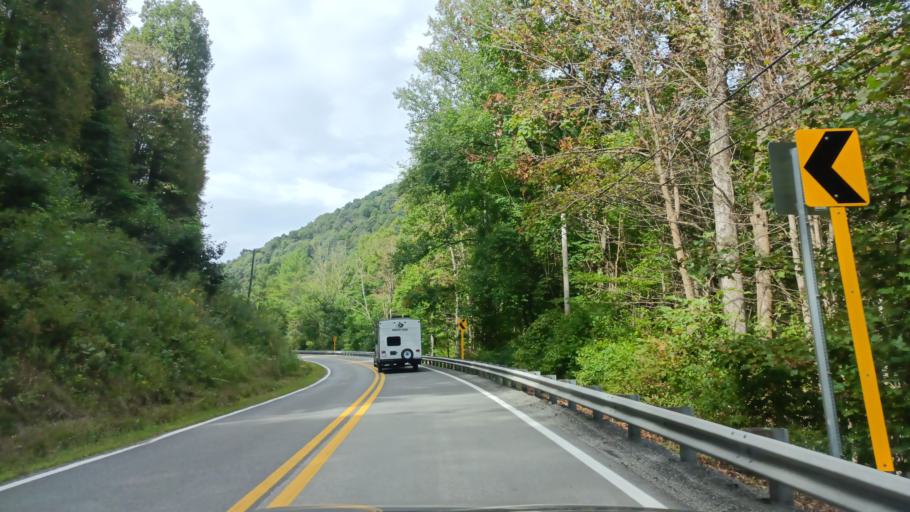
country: US
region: West Virginia
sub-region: Preston County
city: Kingwood
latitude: 39.3262
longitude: -79.6684
